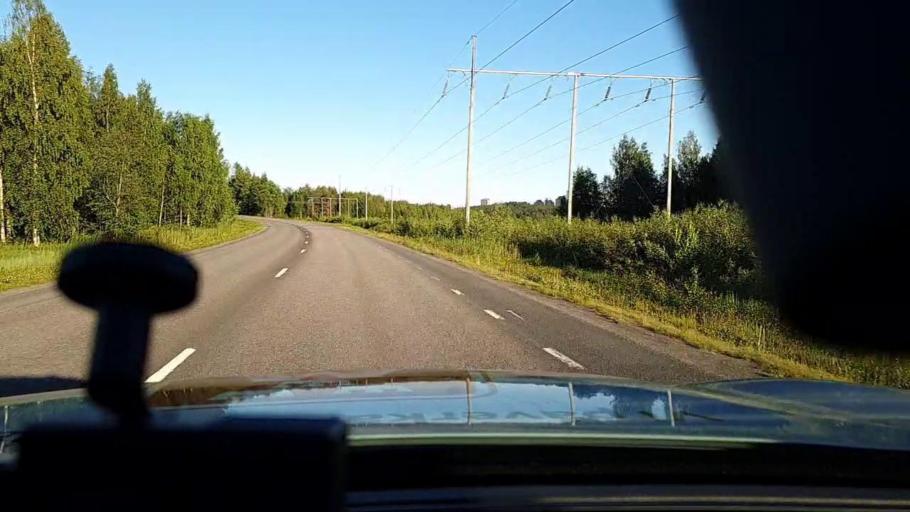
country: SE
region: Norrbotten
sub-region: Lulea Kommun
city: Lulea
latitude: 65.6090
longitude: 22.1671
